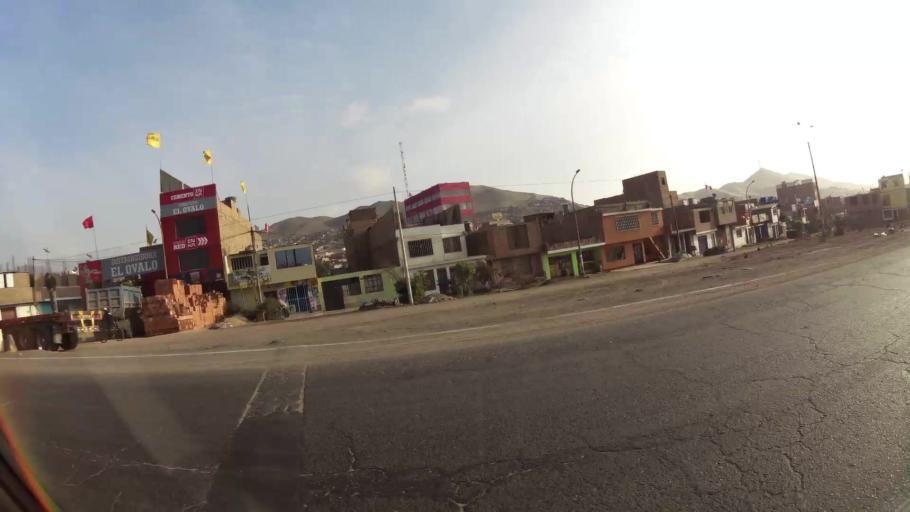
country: PE
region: Lima
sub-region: Lima
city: Santa Rosa
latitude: -11.7760
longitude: -77.1642
